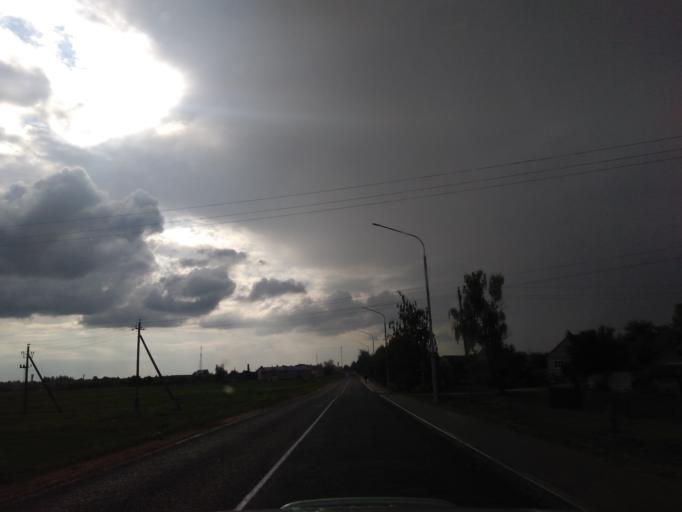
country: BY
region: Minsk
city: Kapyl'
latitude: 53.1419
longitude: 27.1134
